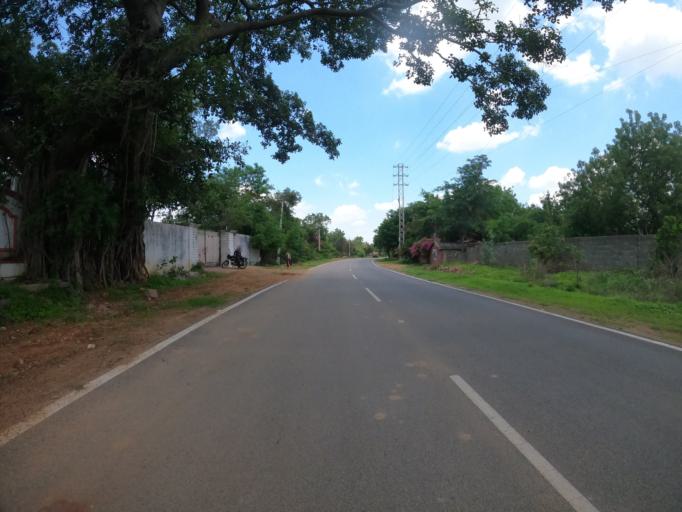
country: IN
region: Telangana
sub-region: Rangareddi
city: Sriramnagar
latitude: 17.3697
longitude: 78.3247
